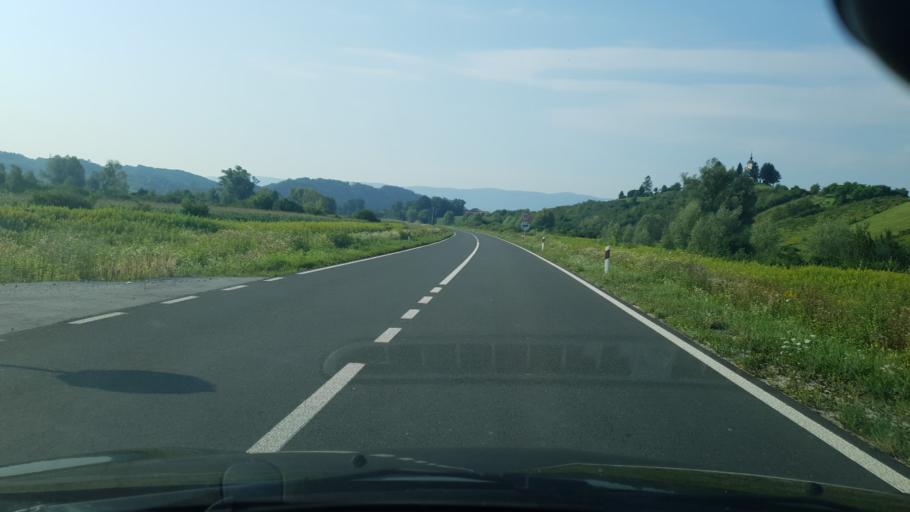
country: HR
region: Krapinsko-Zagorska
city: Zabok
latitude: 46.0440
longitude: 15.9147
